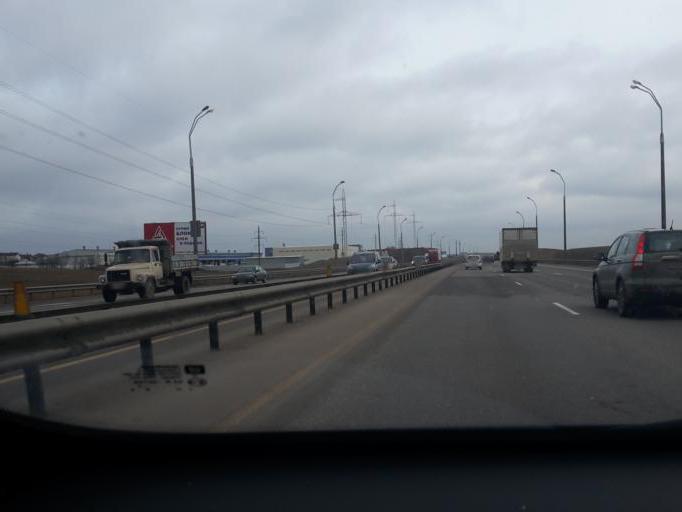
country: BY
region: Minsk
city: Zhdanovichy
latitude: 53.9291
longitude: 27.4202
